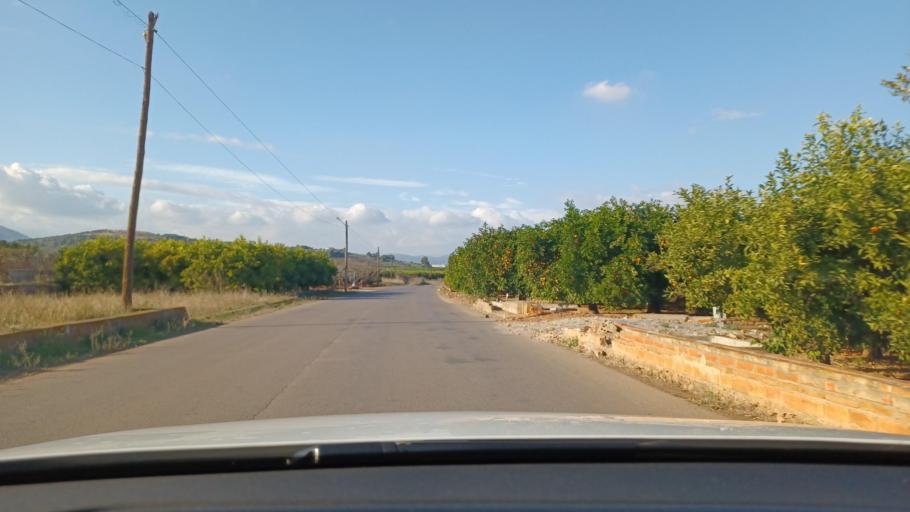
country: ES
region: Valencia
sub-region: Provincia de Castello
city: Betxi
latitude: 39.9351
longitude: -0.2059
